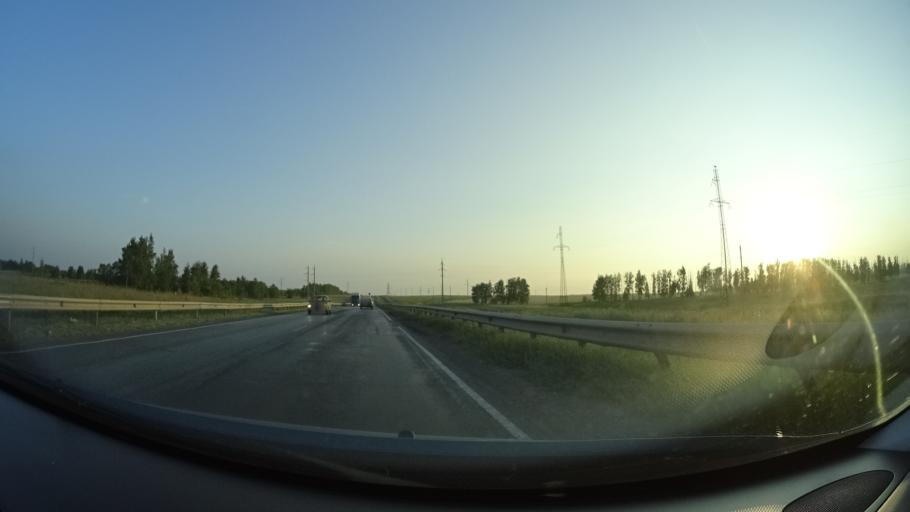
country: RU
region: Samara
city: Sernovodsk
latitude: 53.9408
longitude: 51.3535
